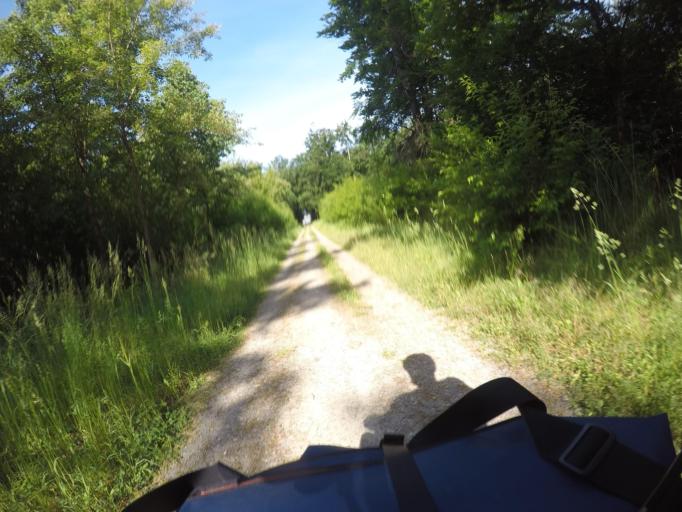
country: DE
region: Baden-Wuerttemberg
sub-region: Karlsruhe Region
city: Rheinstetten
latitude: 48.9348
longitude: 8.3086
